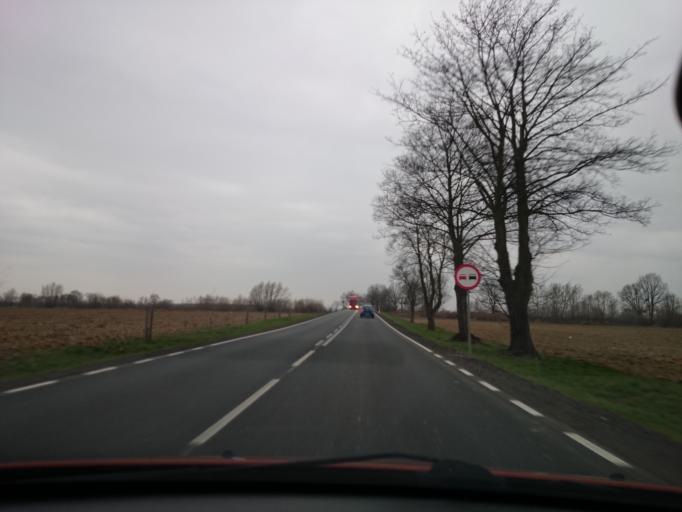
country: PL
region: Opole Voivodeship
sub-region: Powiat nyski
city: Sidzina
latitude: 50.5857
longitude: 17.4780
